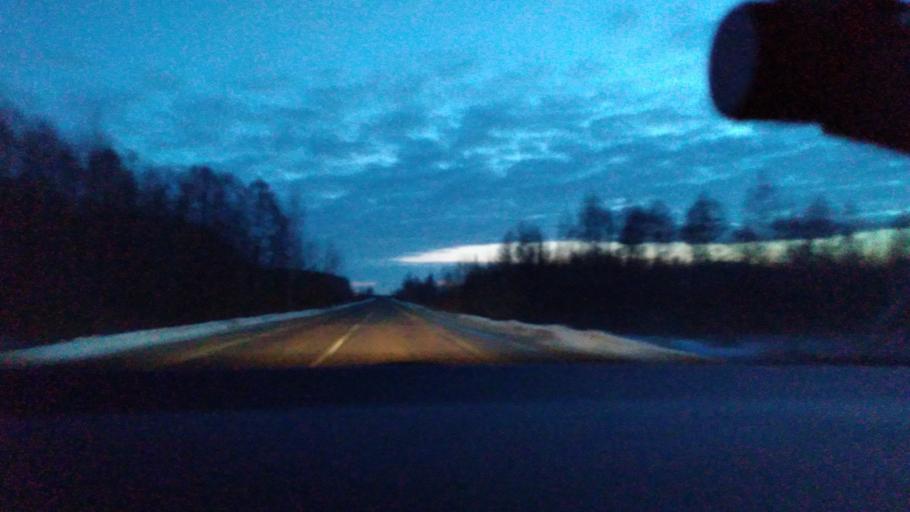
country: RU
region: Moskovskaya
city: Krasnaya Poyma
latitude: 55.1531
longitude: 39.2199
